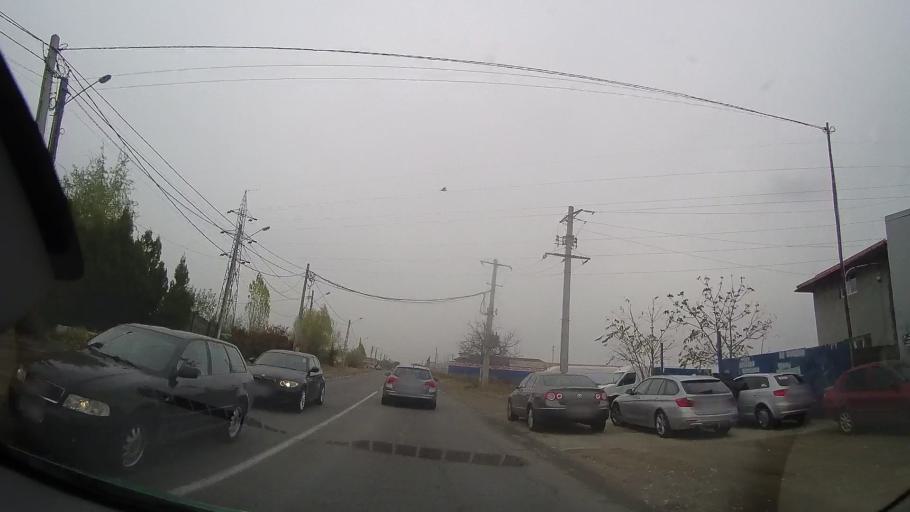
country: RO
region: Prahova
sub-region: Comuna Blejoiu
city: Ploiestiori
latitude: 44.9743
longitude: 26.0188
